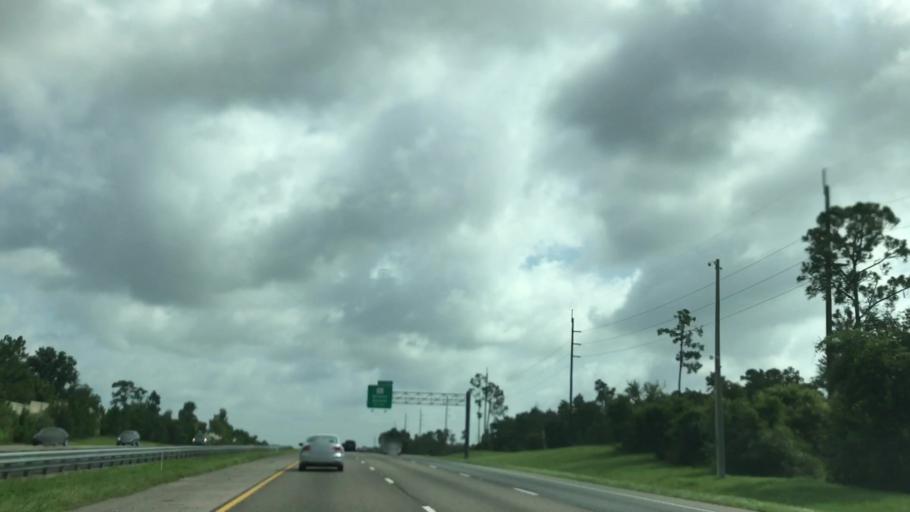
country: US
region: Florida
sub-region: Volusia County
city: Orange City
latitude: 28.9414
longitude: -81.2617
